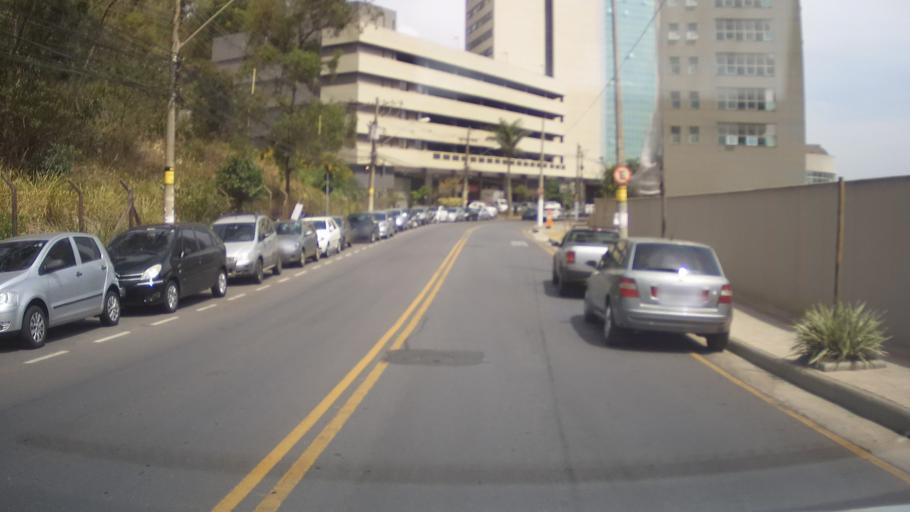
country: BR
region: Minas Gerais
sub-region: Belo Horizonte
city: Belo Horizonte
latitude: -19.9857
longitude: -43.9459
